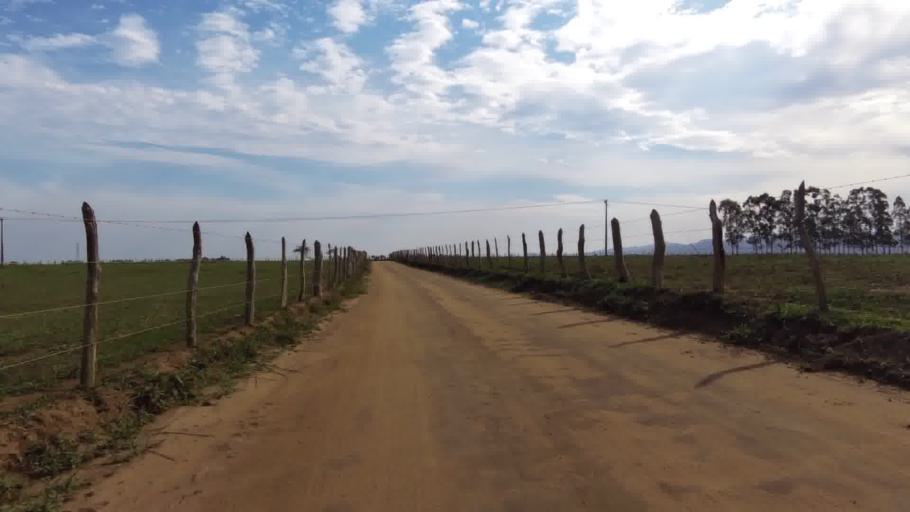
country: BR
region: Espirito Santo
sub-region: Piuma
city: Piuma
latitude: -20.8224
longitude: -40.7459
